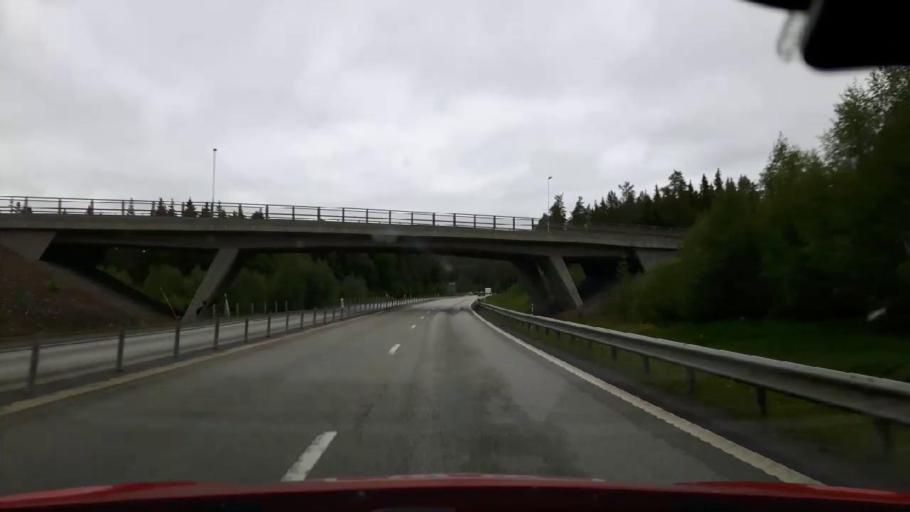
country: SE
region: Jaemtland
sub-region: OEstersunds Kommun
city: Ostersund
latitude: 63.1881
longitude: 14.6898
